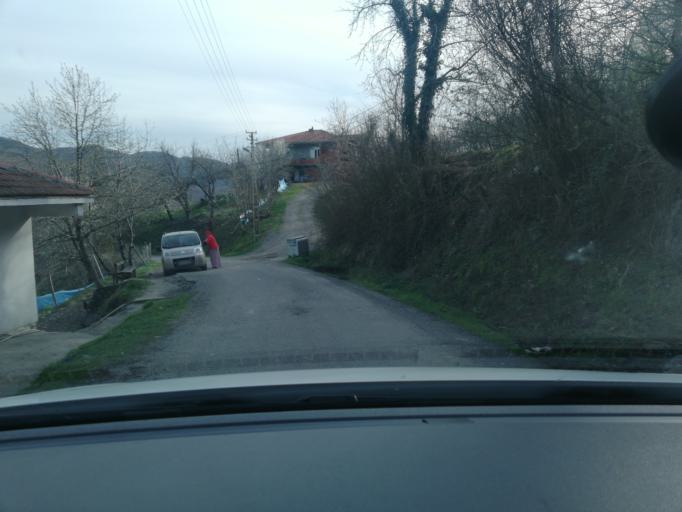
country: TR
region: Zonguldak
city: Kozlu
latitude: 41.3559
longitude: 31.6444
